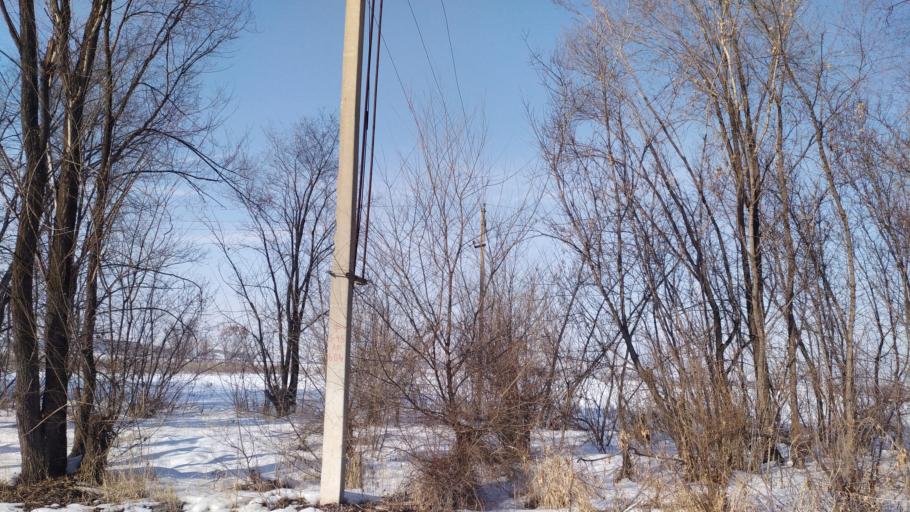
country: KZ
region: Almaty Oblysy
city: Burunday
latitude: 43.2380
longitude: 76.4170
